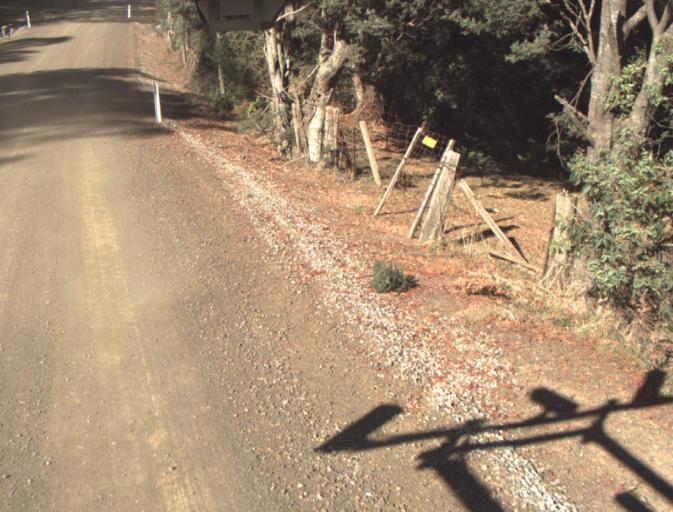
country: AU
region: Tasmania
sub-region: Launceston
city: Newstead
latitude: -41.2960
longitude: 147.3375
